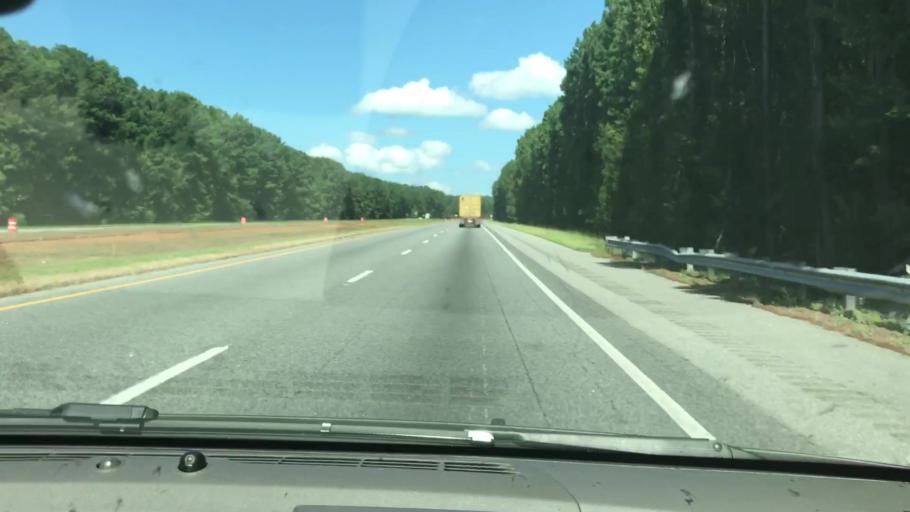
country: US
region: Georgia
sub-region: Harris County
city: Hamilton
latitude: 32.6973
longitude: -84.9998
